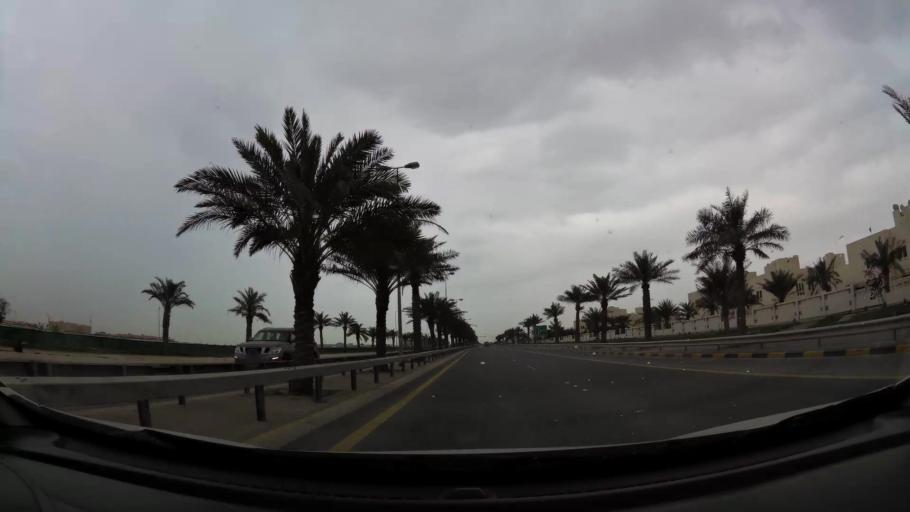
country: BH
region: Northern
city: Ar Rifa'
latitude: 26.1049
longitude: 50.5412
